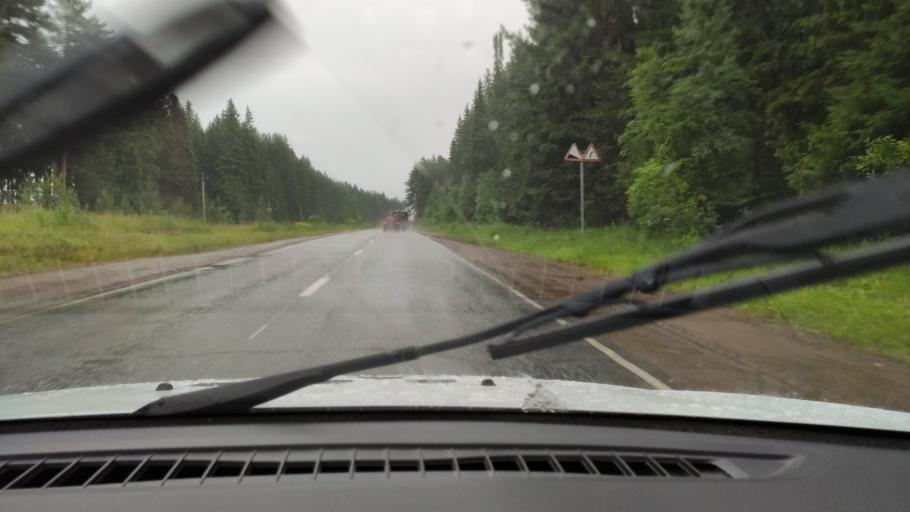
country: RU
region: Udmurtiya
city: Votkinsk
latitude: 57.0758
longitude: 54.0314
